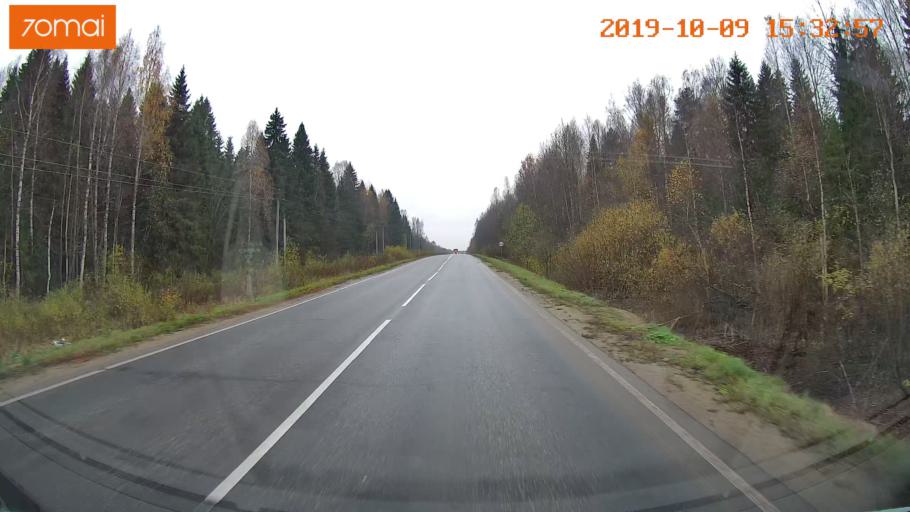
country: RU
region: Kostroma
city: Oktyabr'skiy
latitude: 57.9584
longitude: 41.2691
